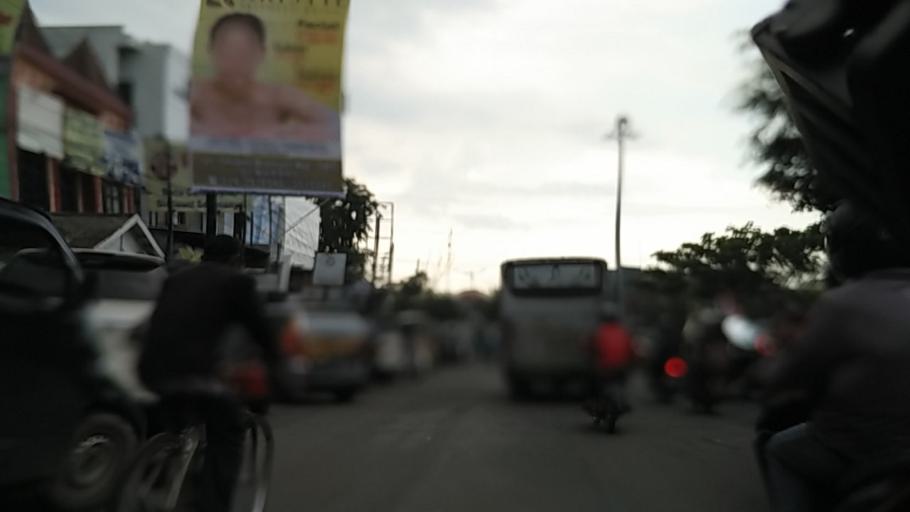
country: ID
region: Central Java
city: Semarang
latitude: -6.9812
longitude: 110.4004
